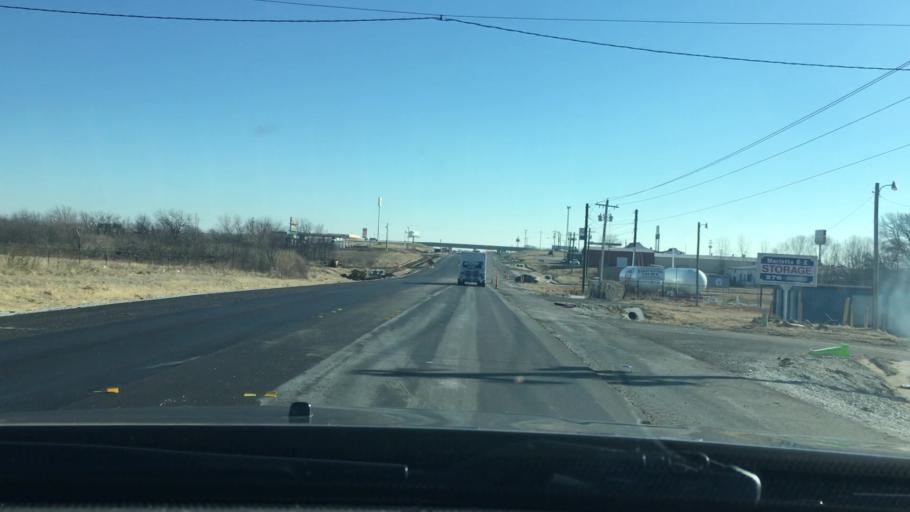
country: US
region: Oklahoma
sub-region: Love County
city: Marietta
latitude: 33.9404
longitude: -97.1419
